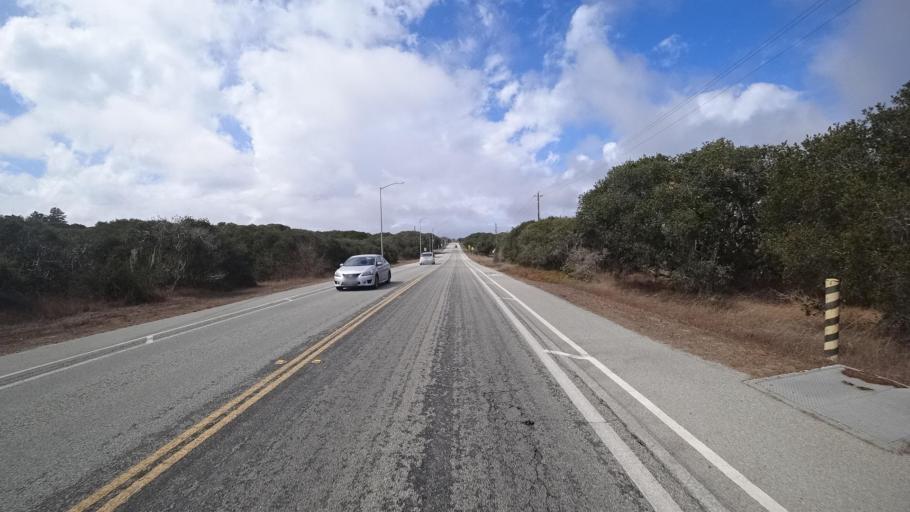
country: US
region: California
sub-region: Monterey County
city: Marina
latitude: 36.6553
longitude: -121.7711
